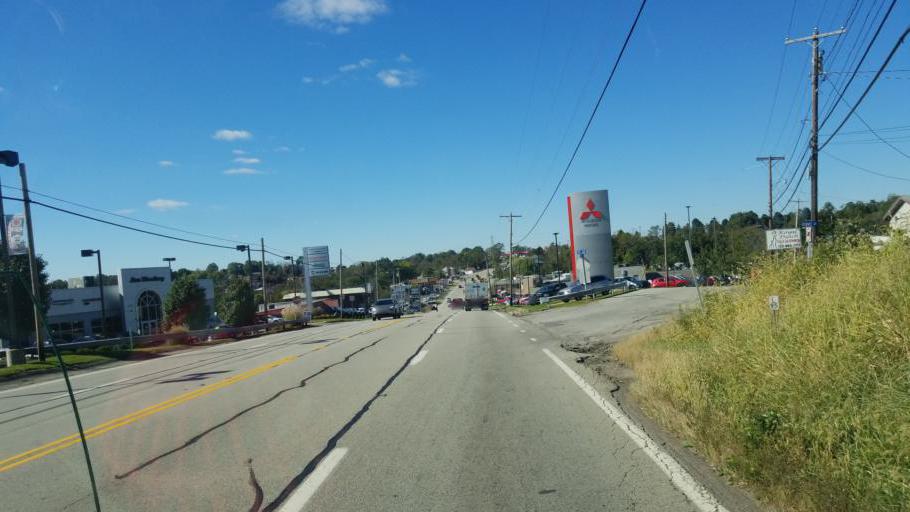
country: US
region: Pennsylvania
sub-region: Westmoreland County
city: Trafford
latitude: 40.3416
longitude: -79.7582
